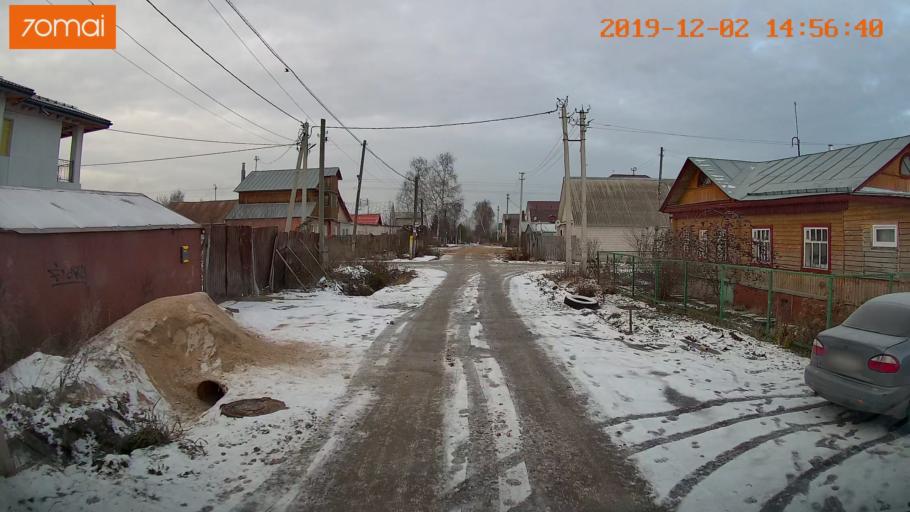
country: RU
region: Ivanovo
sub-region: Gorod Ivanovo
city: Ivanovo
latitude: 56.9728
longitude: 41.0152
